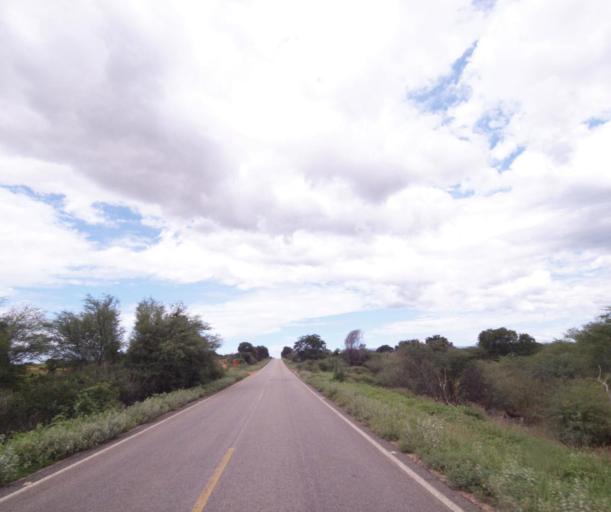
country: BR
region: Bahia
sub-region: Palmas De Monte Alto
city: Palmas de Monte Alto
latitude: -14.2599
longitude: -43.2899
